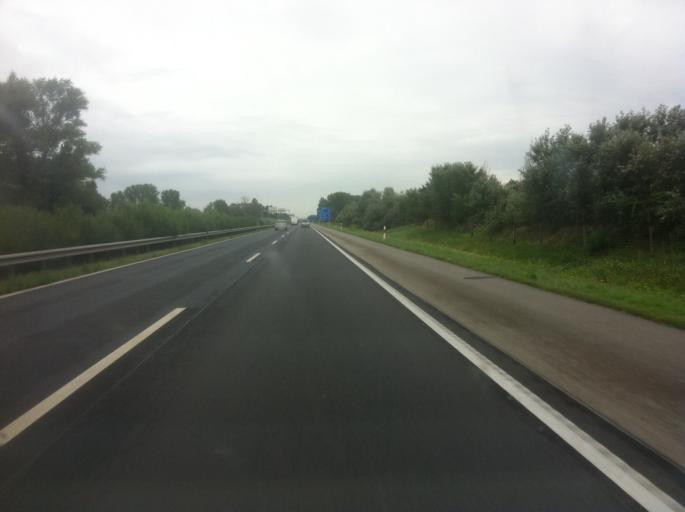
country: HU
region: Pest
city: Gyal
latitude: 47.3896
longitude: 19.1726
